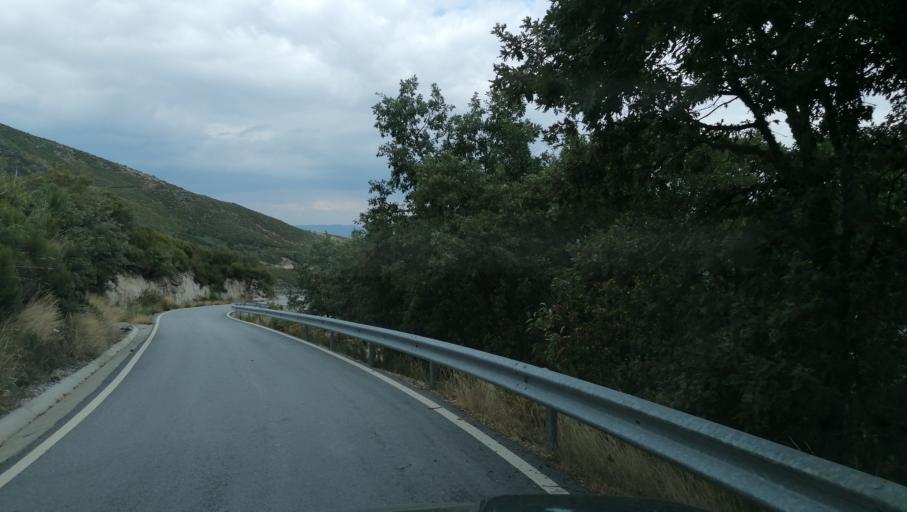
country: PT
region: Vila Real
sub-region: Vila Pouca de Aguiar
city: Vila Pouca de Aguiar
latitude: 41.5509
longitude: -7.6551
